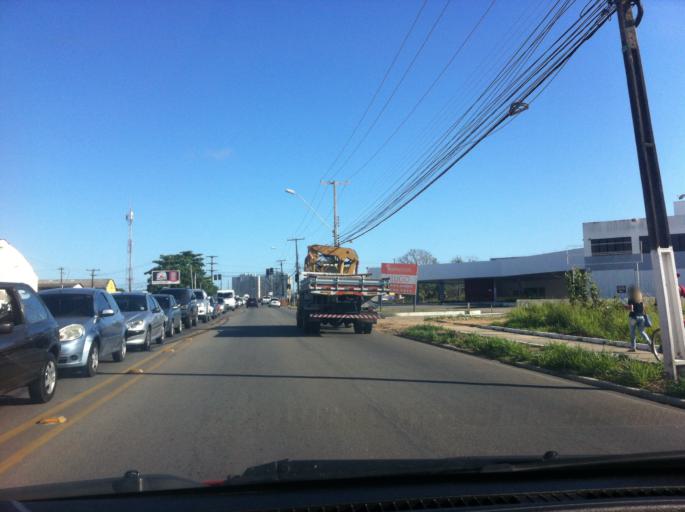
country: BR
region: Alagoas
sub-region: Maceio
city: Maceio
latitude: -9.5849
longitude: -35.7338
